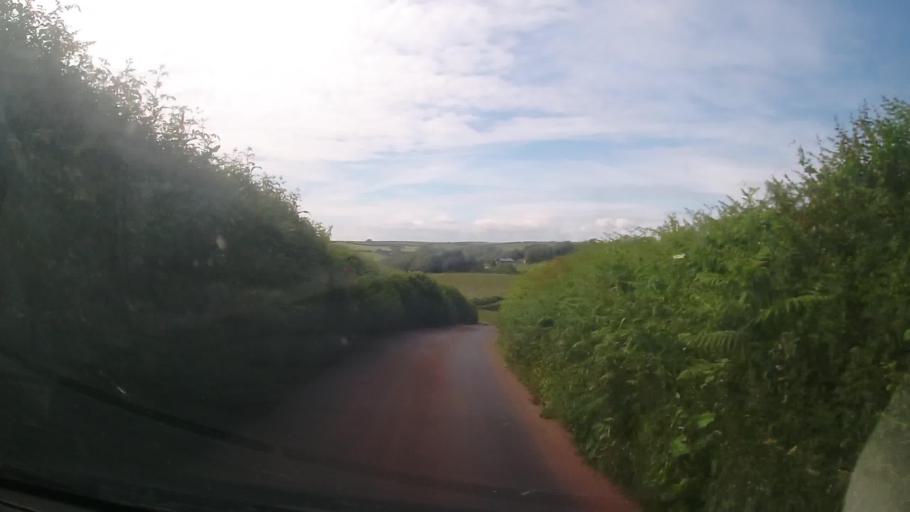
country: GB
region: England
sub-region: Devon
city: Salcombe
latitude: 50.2380
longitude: -3.6766
